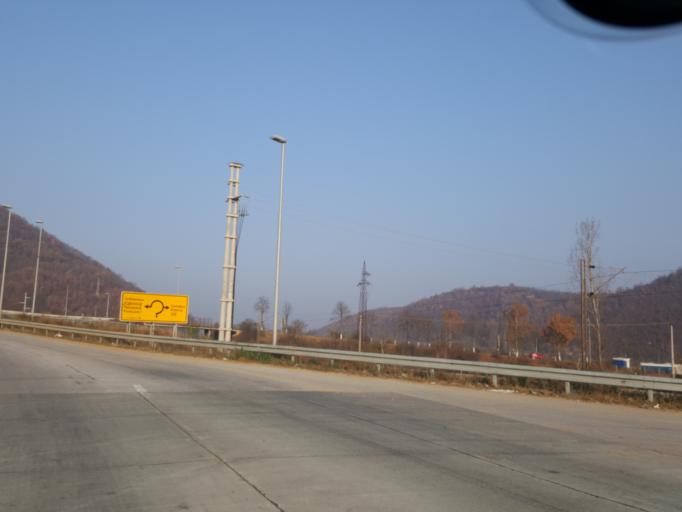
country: RS
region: Central Serbia
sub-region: Jablanicki Okrug
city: Vlasotince
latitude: 42.8863
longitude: 22.0683
